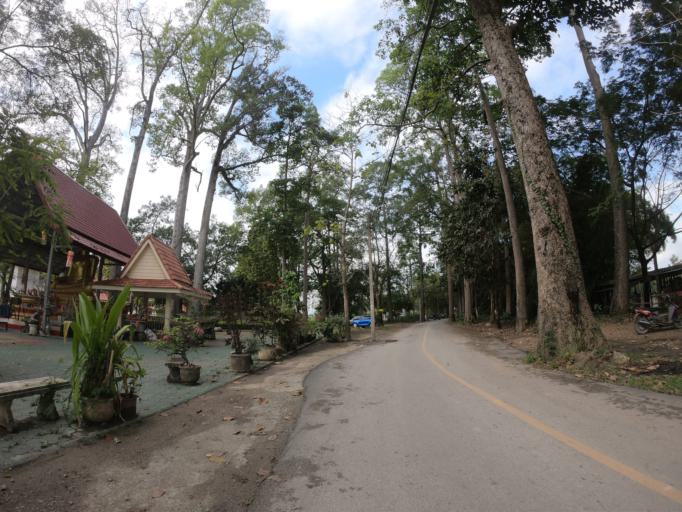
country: TH
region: Chiang Mai
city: San Sai
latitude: 18.8591
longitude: 99.0292
